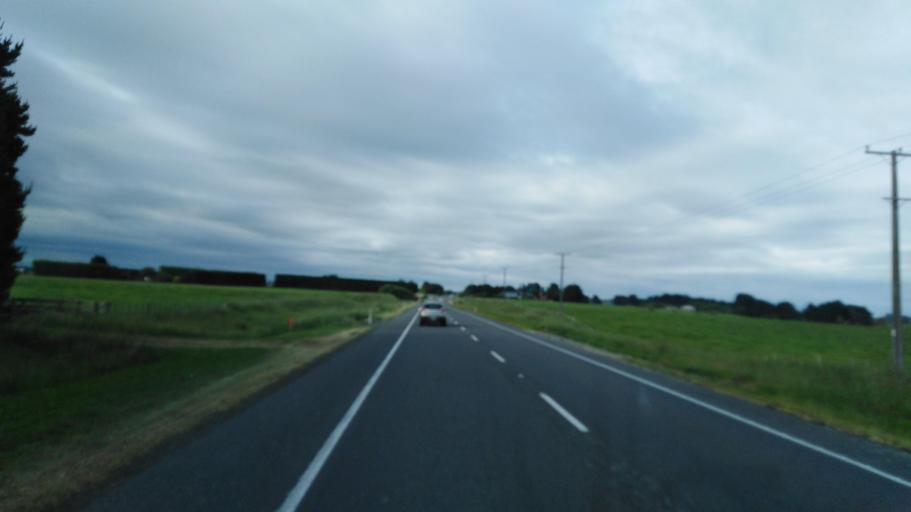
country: NZ
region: Manawatu-Wanganui
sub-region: Rangitikei District
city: Bulls
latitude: -40.2497
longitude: 175.3962
